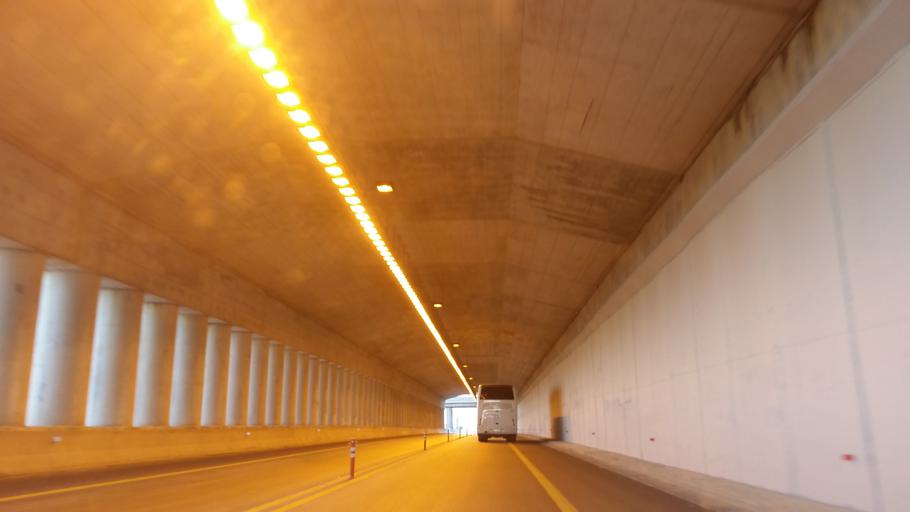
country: GR
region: Peloponnese
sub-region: Nomos Korinthias
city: Xylokastro
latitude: 38.0720
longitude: 22.6319
